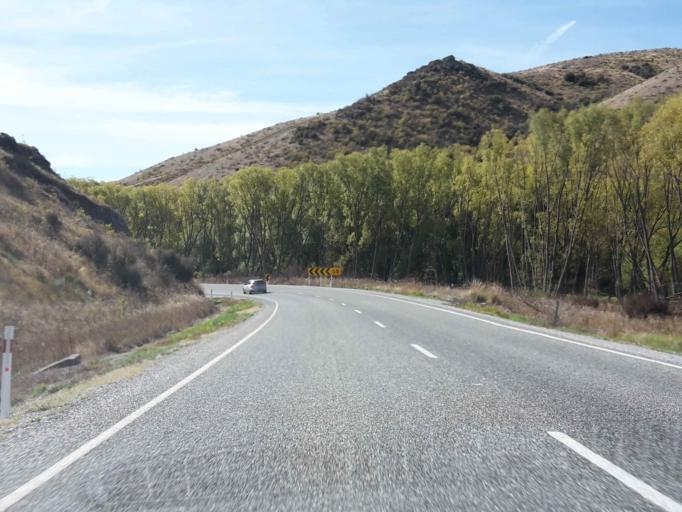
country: NZ
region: Otago
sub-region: Queenstown-Lakes District
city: Wanaka
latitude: -44.7975
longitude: 169.5081
